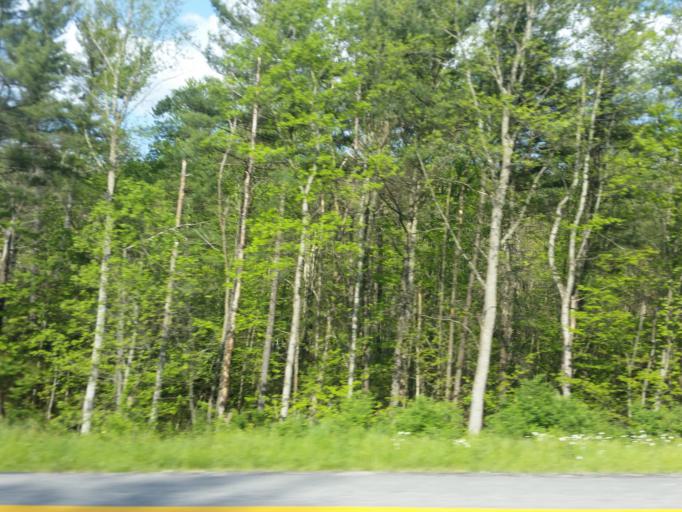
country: US
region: West Virginia
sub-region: Raleigh County
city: Shady Spring
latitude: 37.6855
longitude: -81.1282
